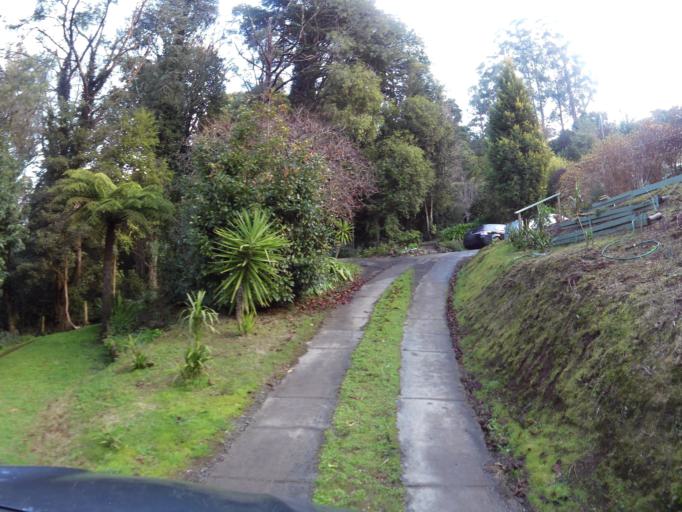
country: AU
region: Victoria
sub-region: Yarra Ranges
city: Kallista
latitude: -37.8791
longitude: 145.3696
